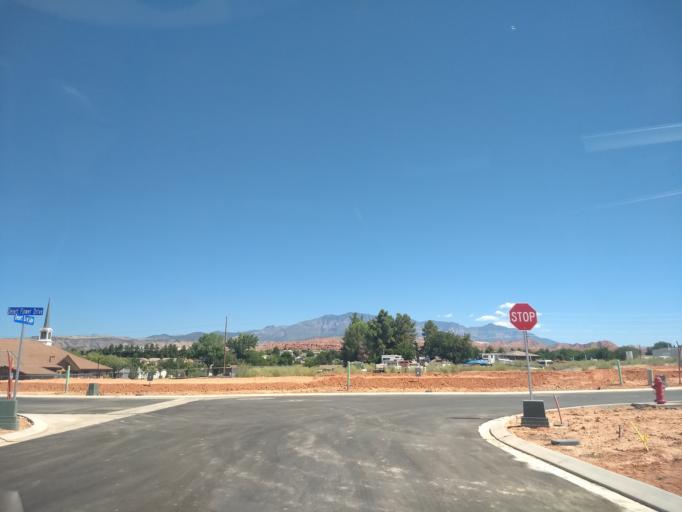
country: US
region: Utah
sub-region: Washington County
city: Washington
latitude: 37.1287
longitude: -113.4988
